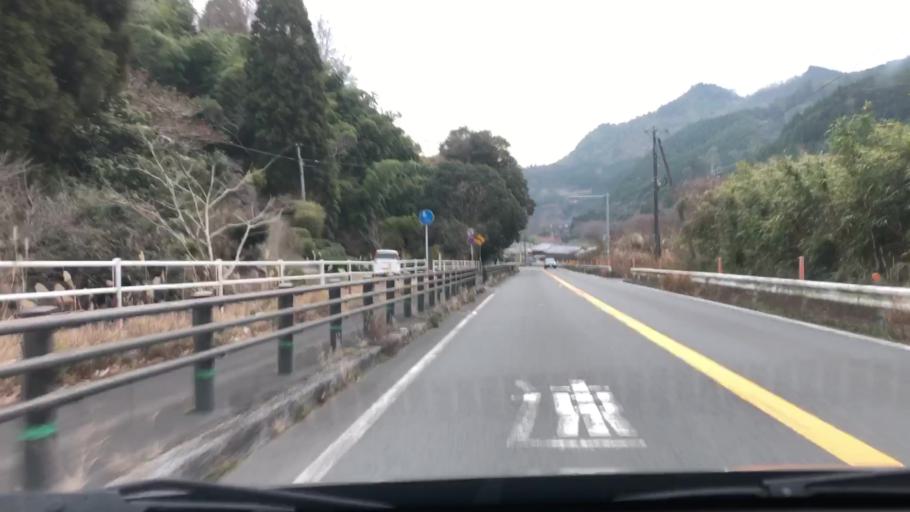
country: JP
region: Oita
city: Saiki
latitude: 32.9903
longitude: 131.8317
